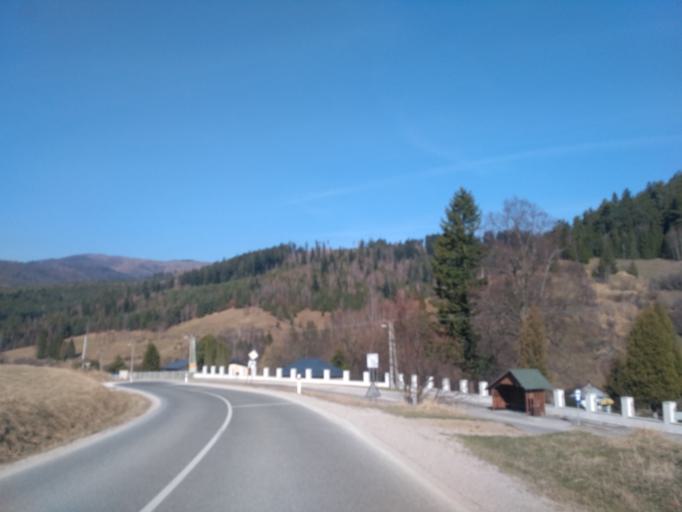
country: SK
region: Kosicky
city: Medzev
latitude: 48.7278
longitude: 20.7279
